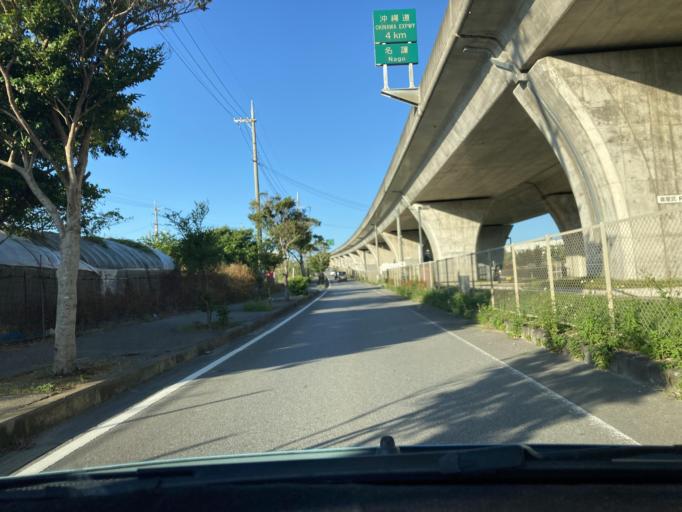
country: JP
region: Okinawa
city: Tomigusuku
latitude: 26.1874
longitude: 127.7373
